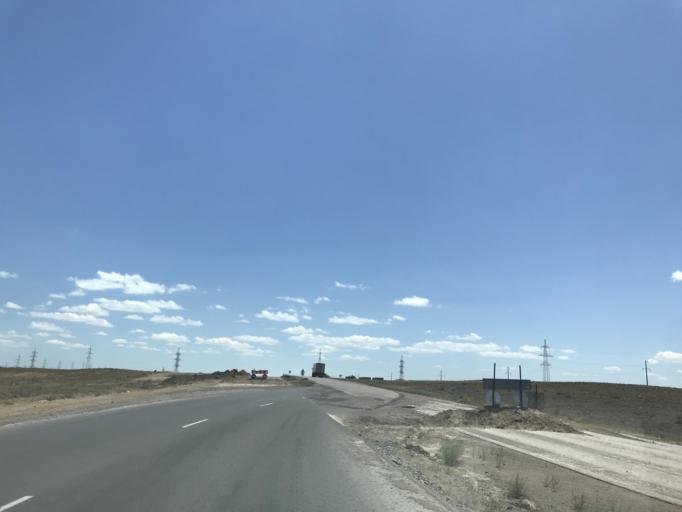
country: KZ
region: Almaty Oblysy
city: Ulken
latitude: 45.2165
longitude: 73.8672
